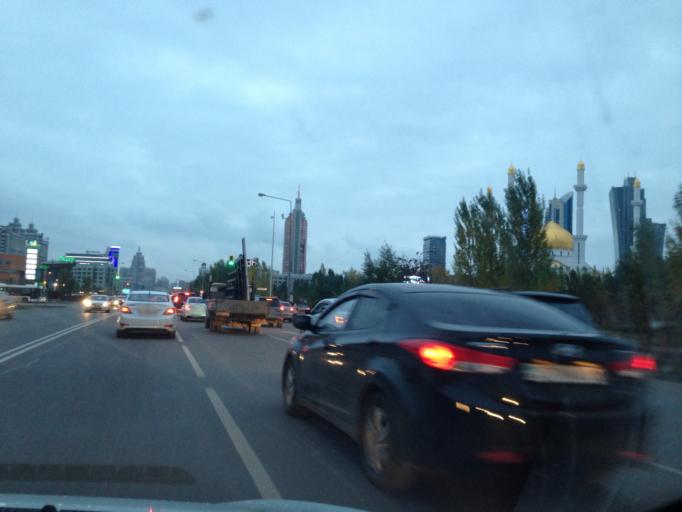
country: KZ
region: Astana Qalasy
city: Astana
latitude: 51.1245
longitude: 71.4132
